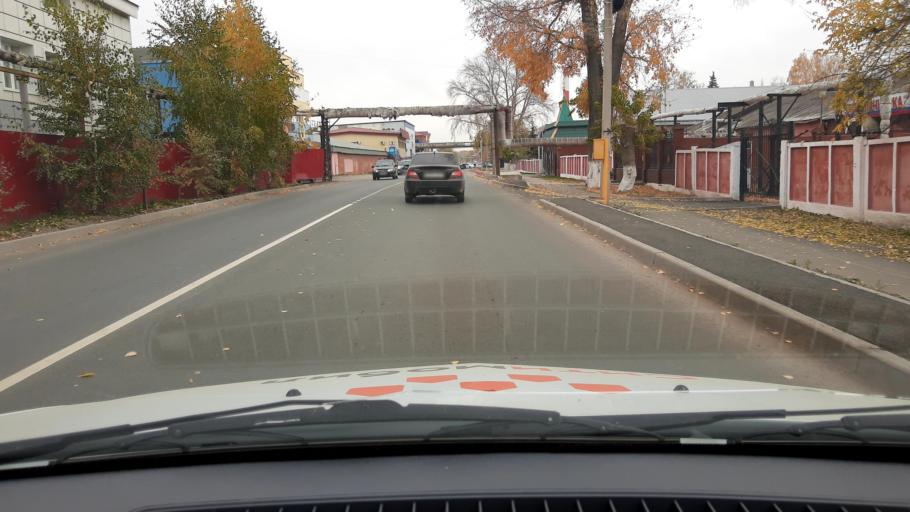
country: RU
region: Bashkortostan
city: Ufa
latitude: 54.7872
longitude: 56.0611
